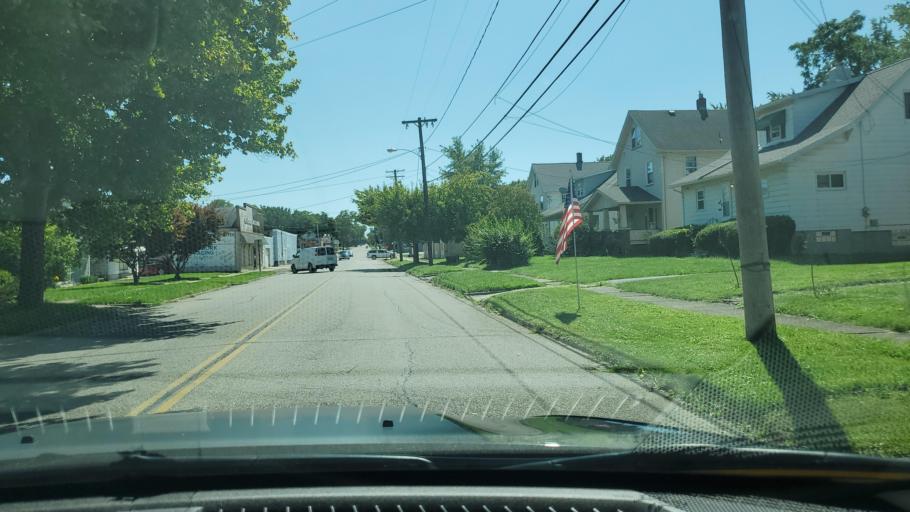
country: US
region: Ohio
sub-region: Mahoning County
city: Struthers
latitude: 41.0572
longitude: -80.6035
